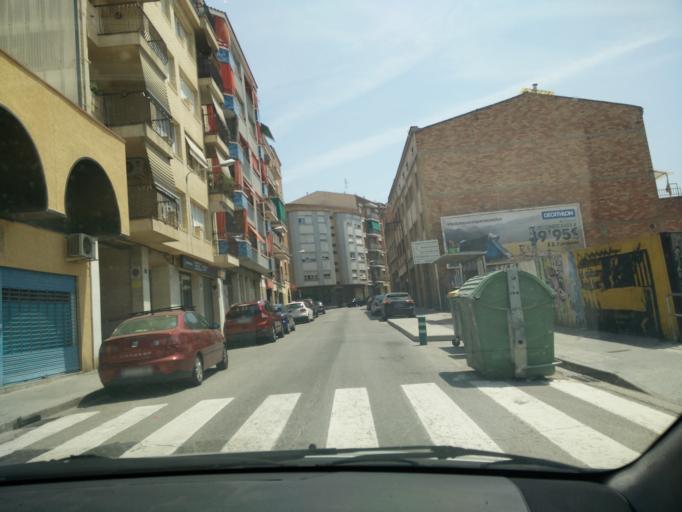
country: ES
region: Catalonia
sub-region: Provincia de Barcelona
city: Manresa
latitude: 41.7275
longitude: 1.8371
